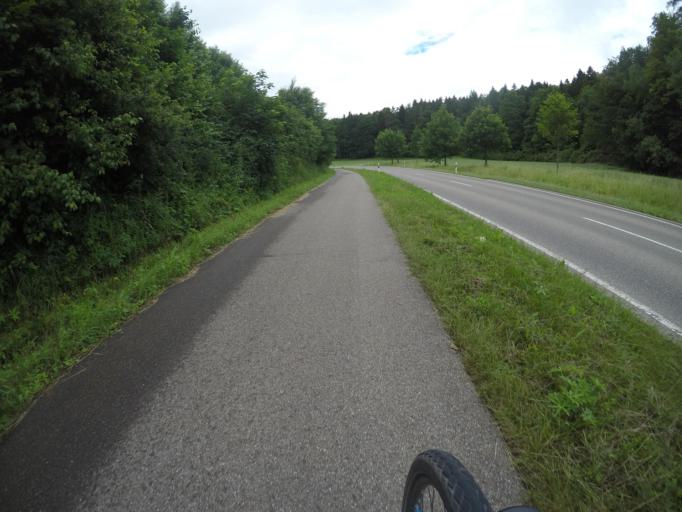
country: DE
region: Baden-Wuerttemberg
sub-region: Regierungsbezirk Stuttgart
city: Gartringen
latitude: 48.6570
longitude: 8.8815
